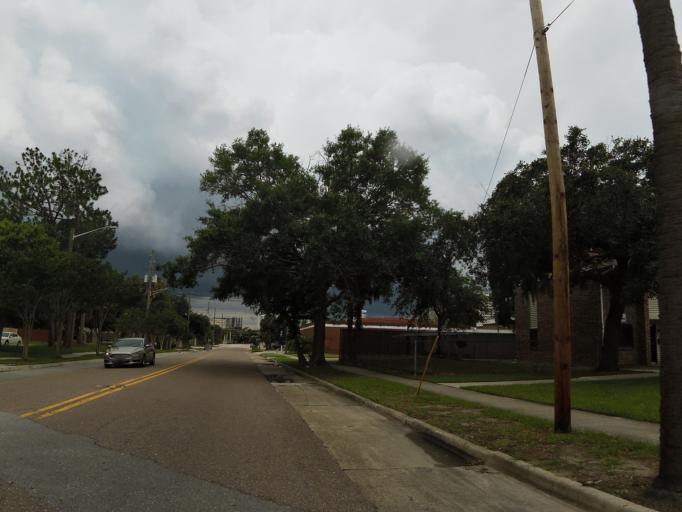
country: US
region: Florida
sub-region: Duval County
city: Jacksonville
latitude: 30.3347
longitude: -81.6505
